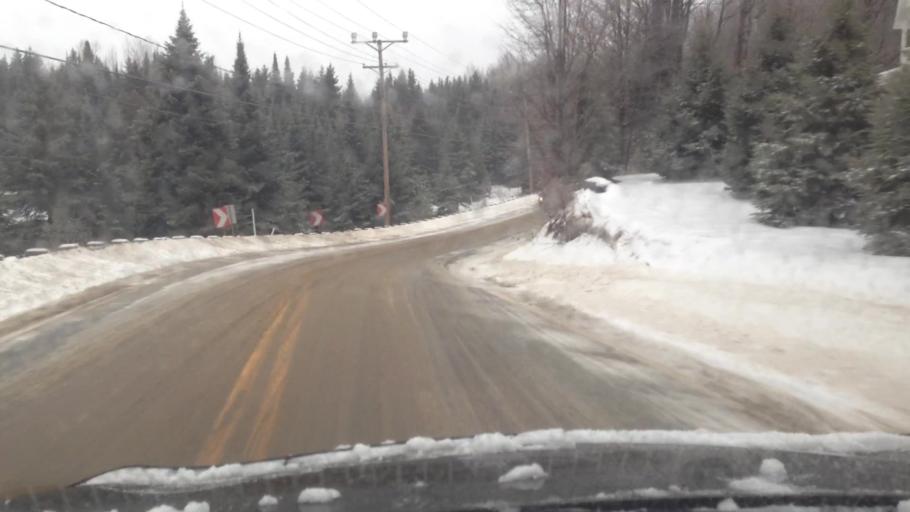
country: CA
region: Quebec
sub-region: Laurentides
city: Mont-Tremblant
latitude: 46.0238
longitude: -74.6067
